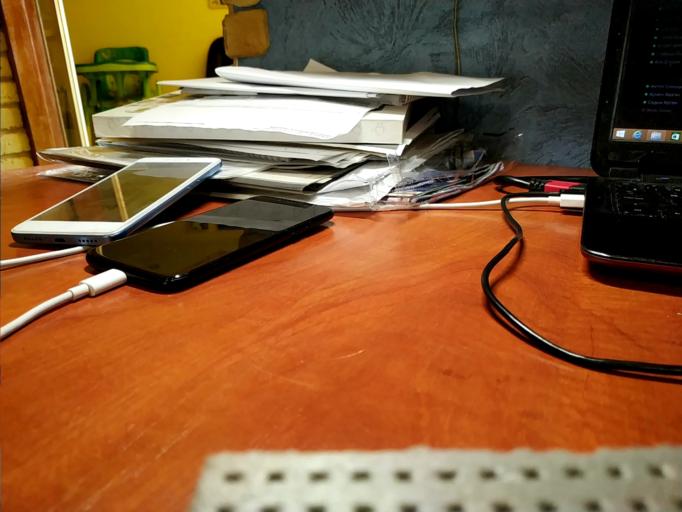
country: RU
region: Tverskaya
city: Spirovo
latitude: 57.4286
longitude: 35.0582
